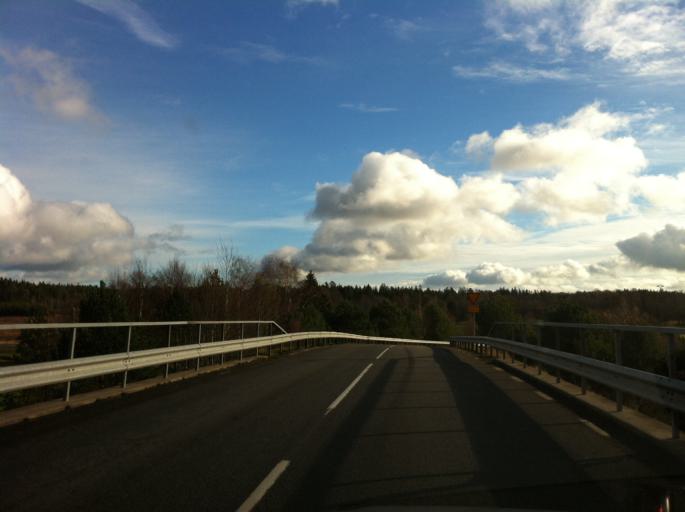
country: SE
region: Kronoberg
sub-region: Almhults Kommun
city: AElmhult
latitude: 56.4837
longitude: 14.1075
